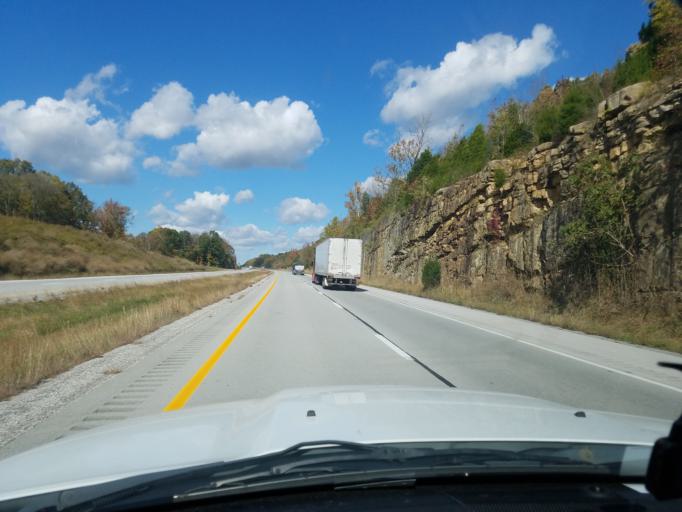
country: US
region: Kentucky
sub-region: Butler County
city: Morgantown
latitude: 37.2462
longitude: -86.7359
